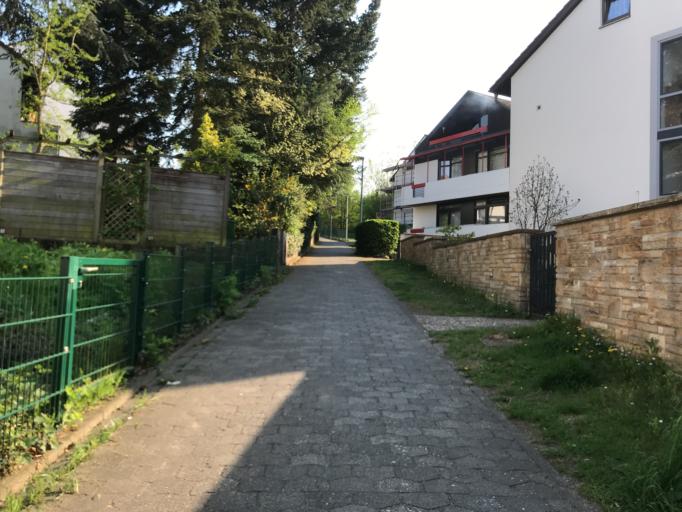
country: DE
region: Rheinland-Pfalz
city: Budenheim
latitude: 50.0188
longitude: 8.2173
